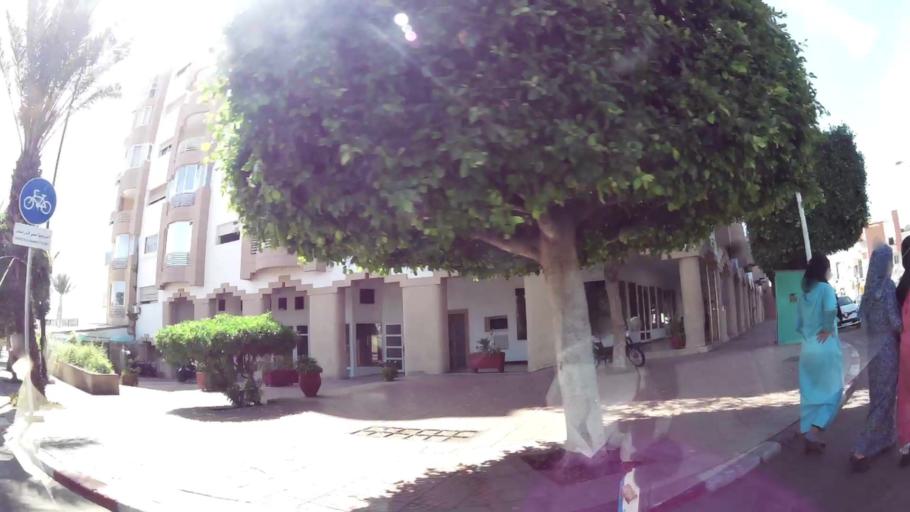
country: MA
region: Souss-Massa-Draa
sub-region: Agadir-Ida-ou-Tnan
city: Agadir
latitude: 30.4084
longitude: -9.5871
